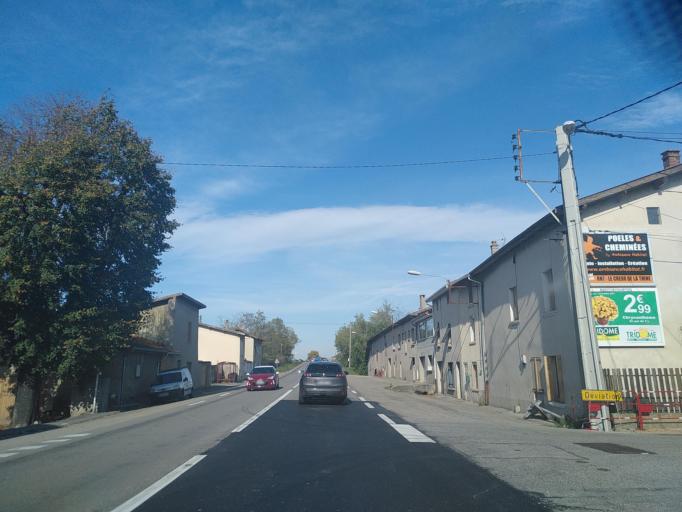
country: FR
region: Rhone-Alpes
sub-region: Departement de la Drome
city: Andancette
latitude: 45.2316
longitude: 4.8182
